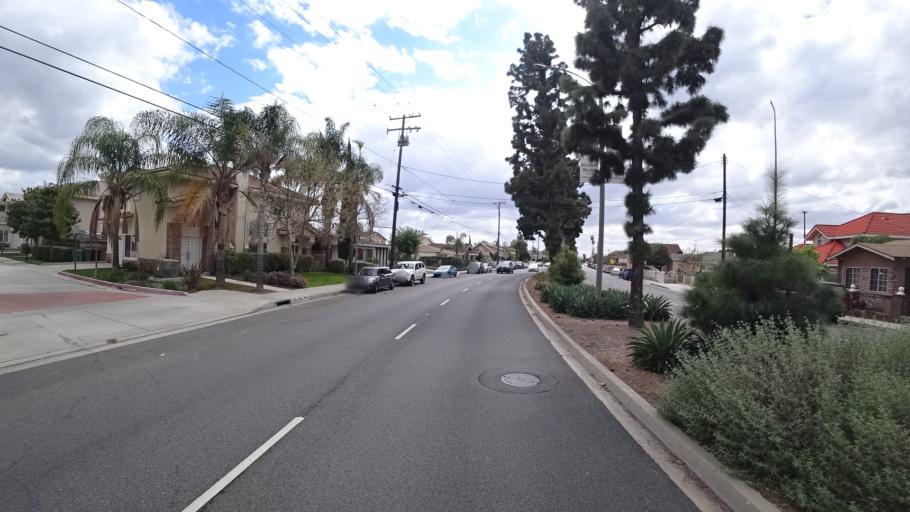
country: US
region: California
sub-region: Los Angeles County
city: Baldwin Park
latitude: 34.0837
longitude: -117.9645
